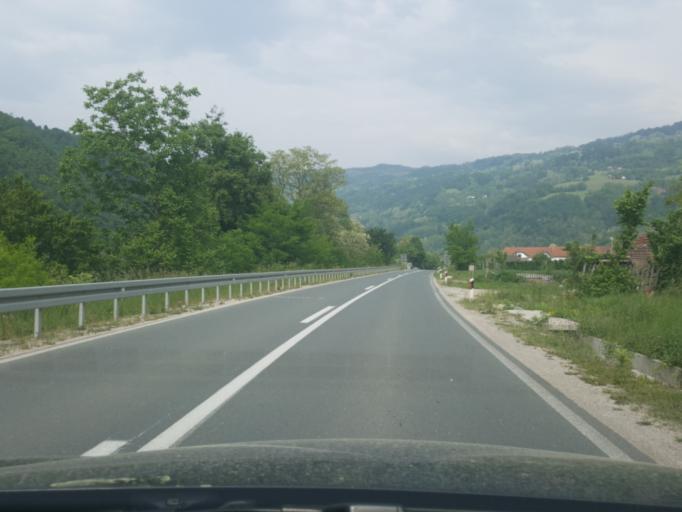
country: RS
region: Central Serbia
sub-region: Zlatiborski Okrug
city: Bajina Basta
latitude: 44.0107
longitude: 19.6054
